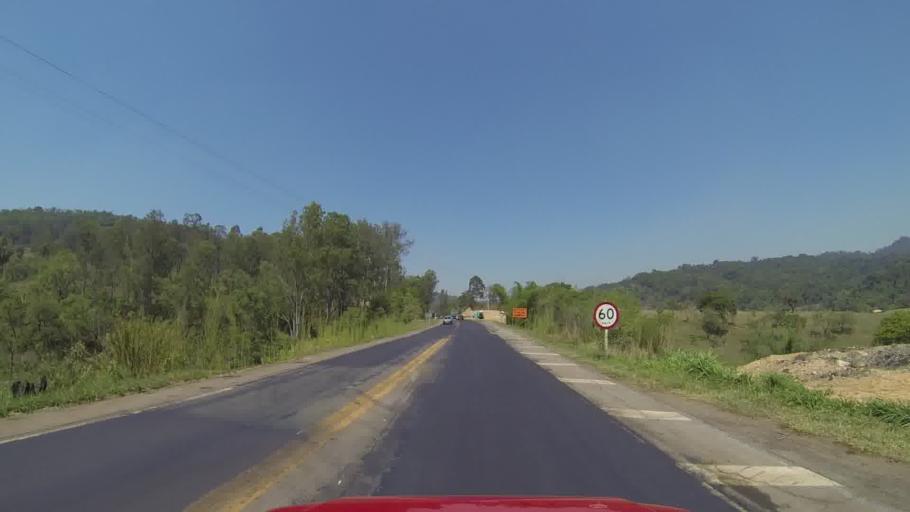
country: BR
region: Minas Gerais
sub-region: Mateus Leme
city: Mateus Leme
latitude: -20.0206
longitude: -44.4982
